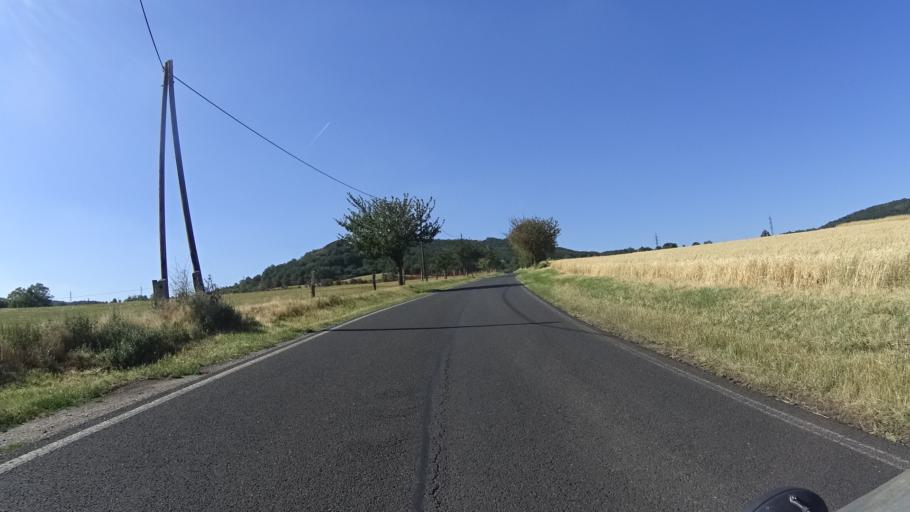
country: CZ
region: Ustecky
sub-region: Okres Litomerice
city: Litomerice
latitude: 50.5580
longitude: 14.1226
